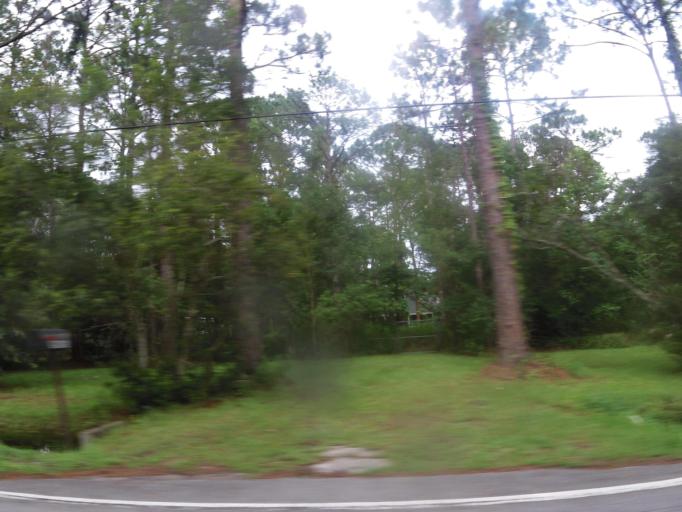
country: US
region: Florida
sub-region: Duval County
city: Jacksonville
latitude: 30.2947
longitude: -81.5294
